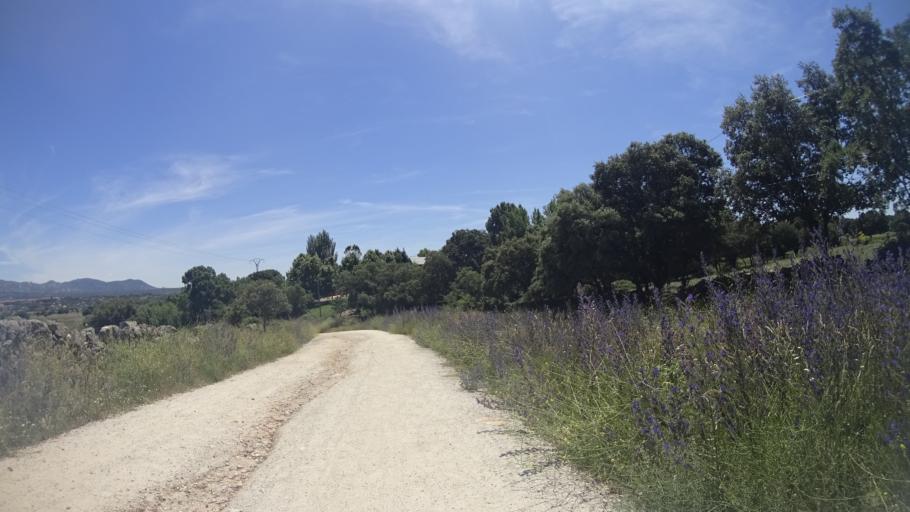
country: ES
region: Madrid
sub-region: Provincia de Madrid
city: Navalquejigo
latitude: 40.6104
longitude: -4.0333
